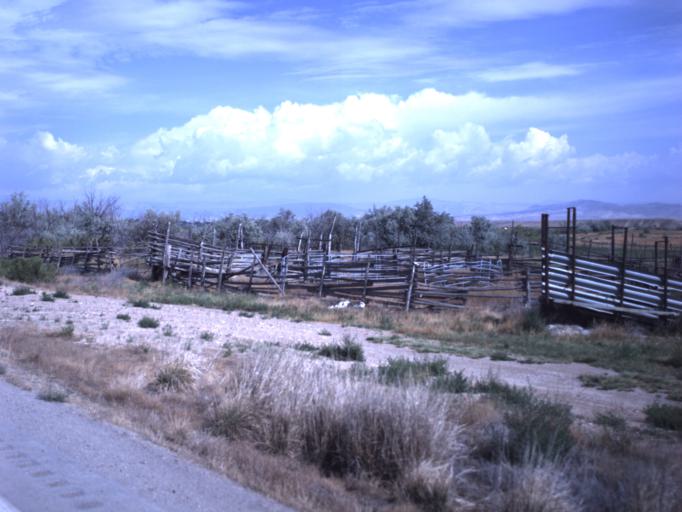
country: US
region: Utah
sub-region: Uintah County
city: Naples
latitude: 40.3831
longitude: -109.4266
